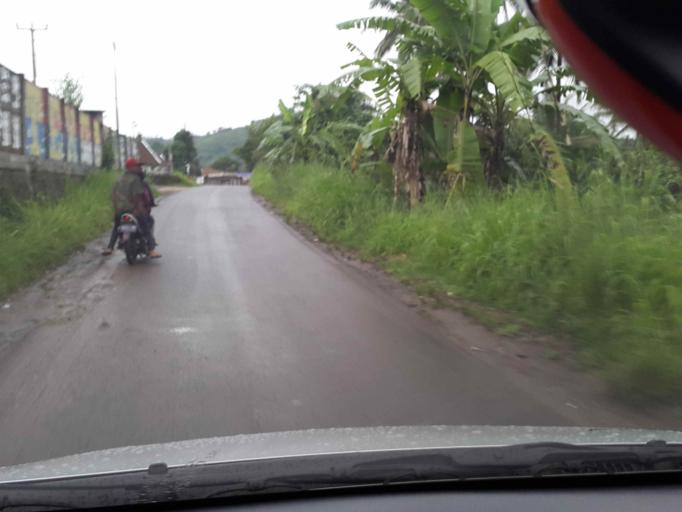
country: ID
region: West Java
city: Sukabumi
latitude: -6.9083
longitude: 106.8609
